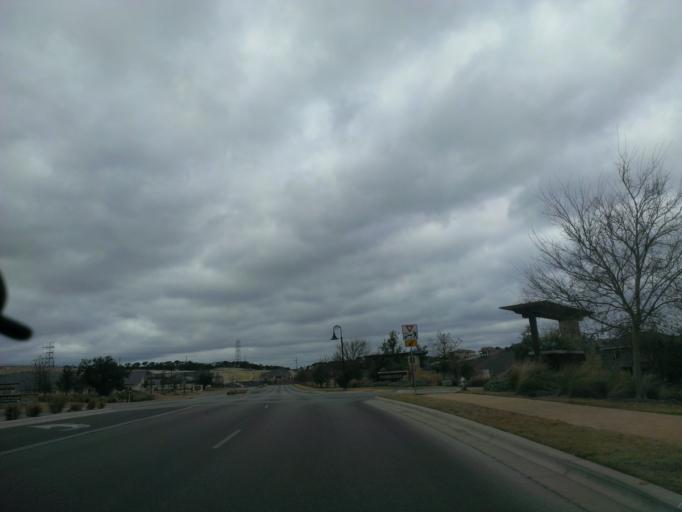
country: US
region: Texas
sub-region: Travis County
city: The Hills
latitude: 30.3507
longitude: -98.0100
